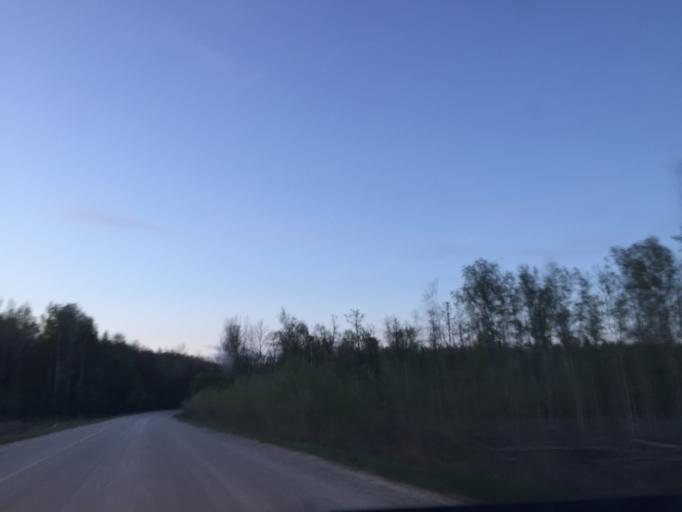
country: LV
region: Bauskas Rajons
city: Bauska
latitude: 56.4785
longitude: 24.1036
